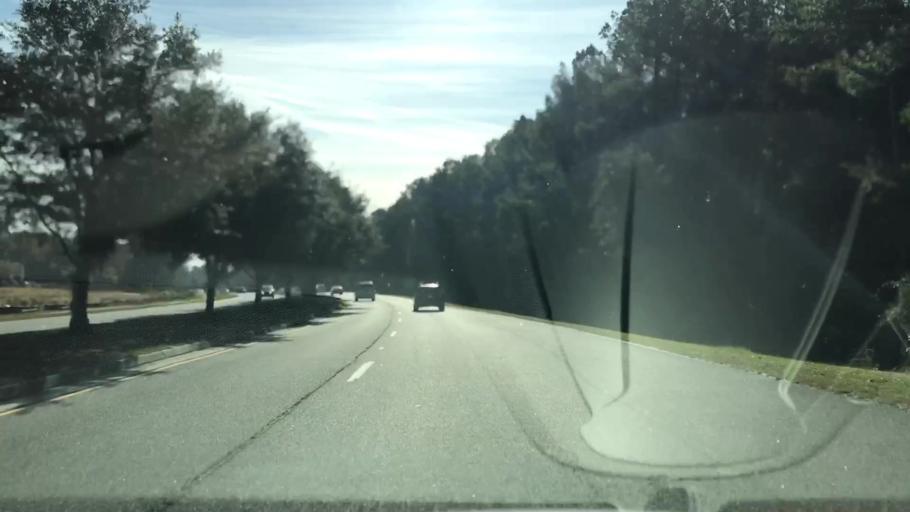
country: US
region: South Carolina
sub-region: Beaufort County
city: Bluffton
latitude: 32.2669
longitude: -80.9136
